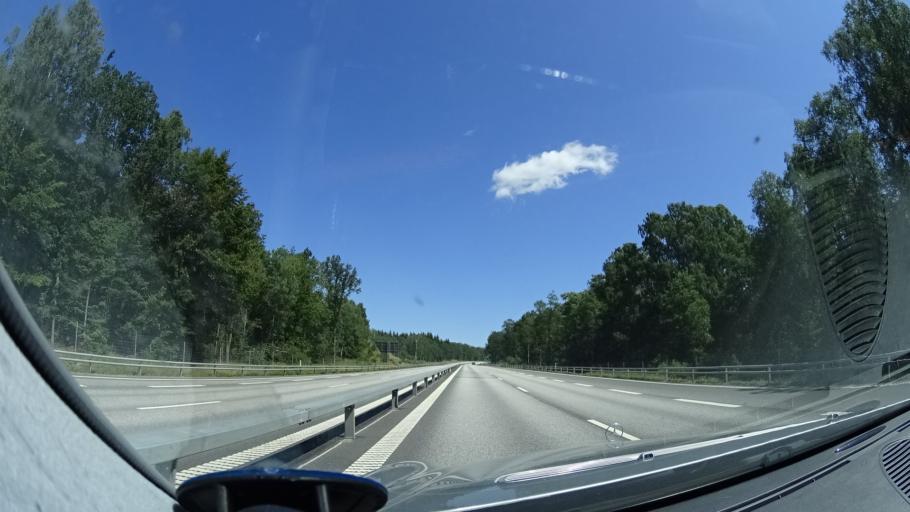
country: SE
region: Skane
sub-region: Horby Kommun
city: Hoerby
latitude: 55.9062
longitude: 13.7440
